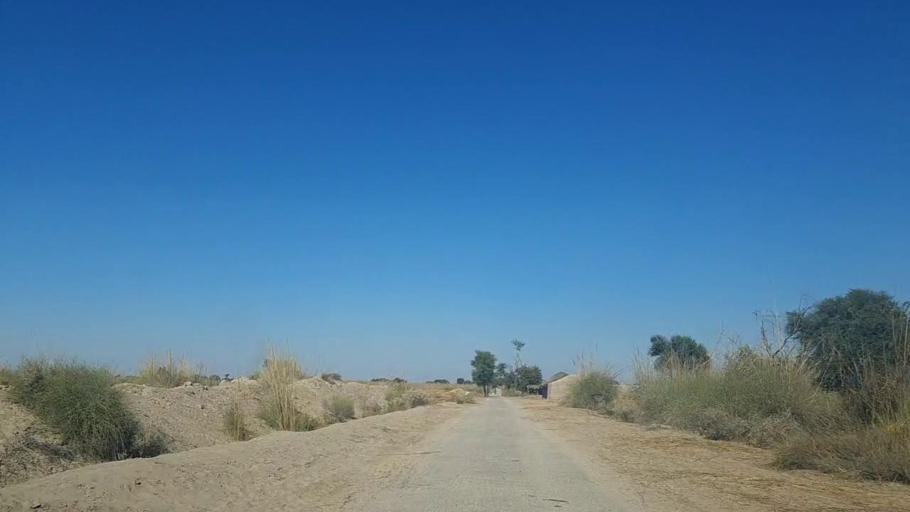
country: PK
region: Sindh
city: Khadro
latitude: 26.2109
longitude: 68.8599
